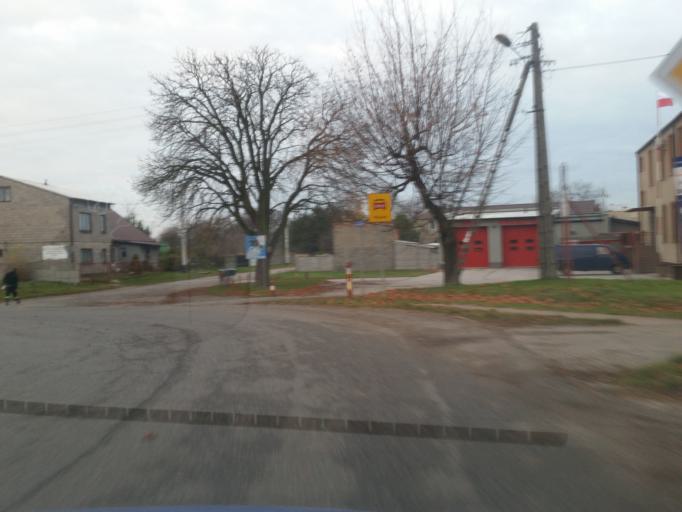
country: PL
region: Silesian Voivodeship
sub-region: Powiat czestochowski
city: Borowno
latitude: 50.9671
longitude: 19.2776
